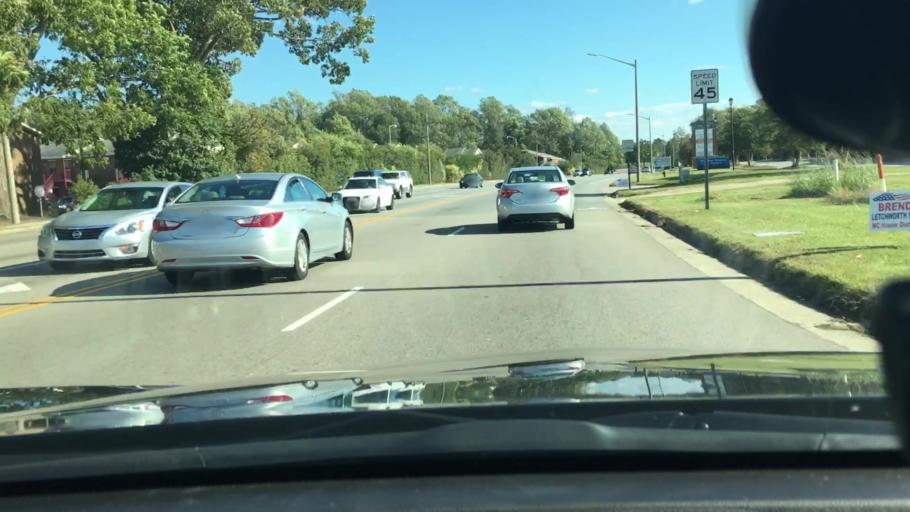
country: US
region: North Carolina
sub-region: Pitt County
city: Summerfield
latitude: 35.5950
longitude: -77.4025
